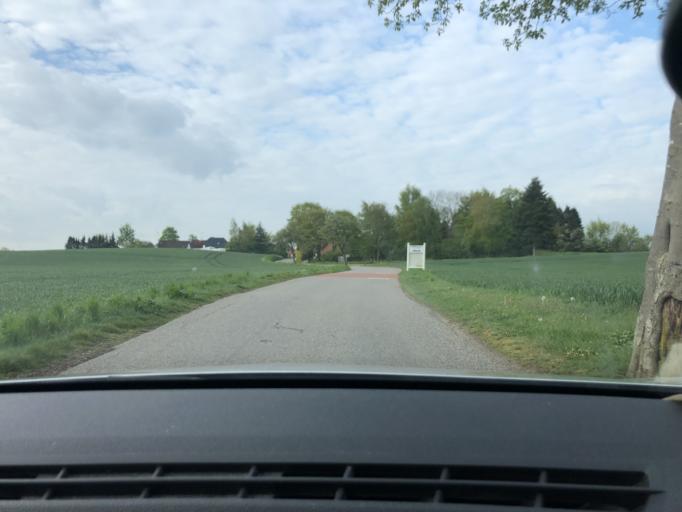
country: DK
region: Zealand
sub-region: Faxe Kommune
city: Ronnede
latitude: 55.2253
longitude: 12.0531
